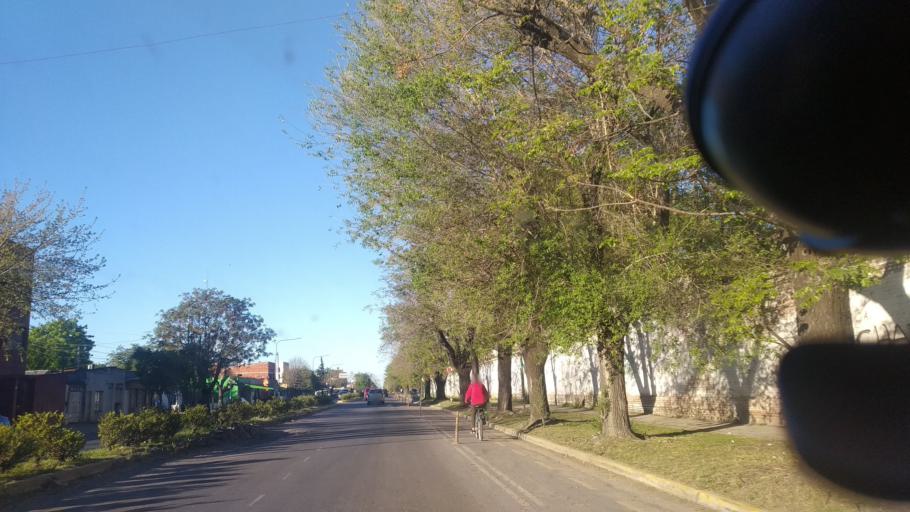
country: AR
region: Buenos Aires
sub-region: Partido de La Plata
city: La Plata
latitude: -34.9555
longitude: -57.9547
